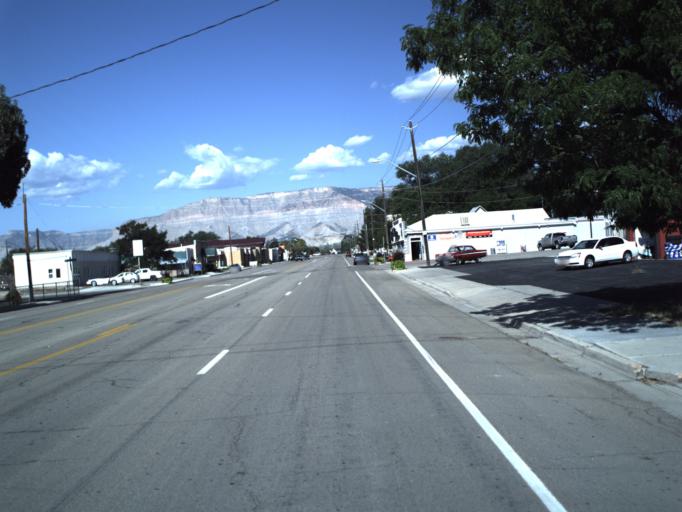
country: US
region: Utah
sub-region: Emery County
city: Castle Dale
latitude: 39.2118
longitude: -111.0149
